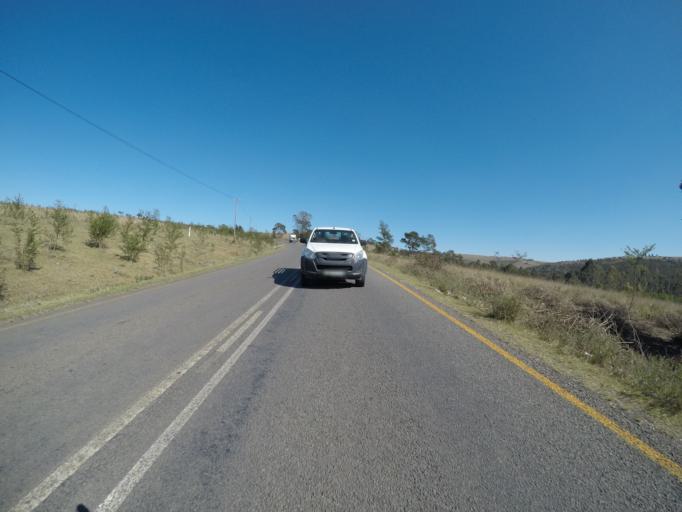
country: ZA
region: Eastern Cape
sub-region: OR Tambo District Municipality
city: Mthatha
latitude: -31.8069
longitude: 28.7620
